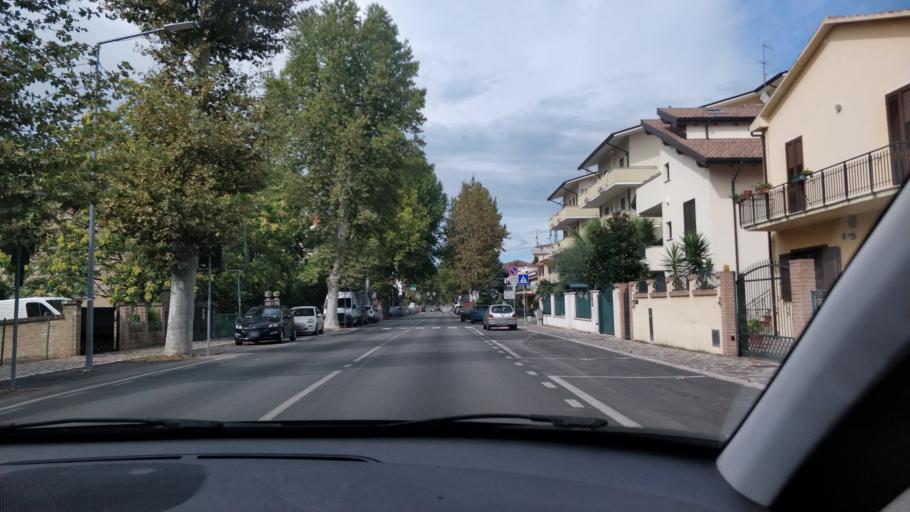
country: IT
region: Abruzzo
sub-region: Provincia di Chieti
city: Sambuceto
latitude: 42.4231
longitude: 14.1839
